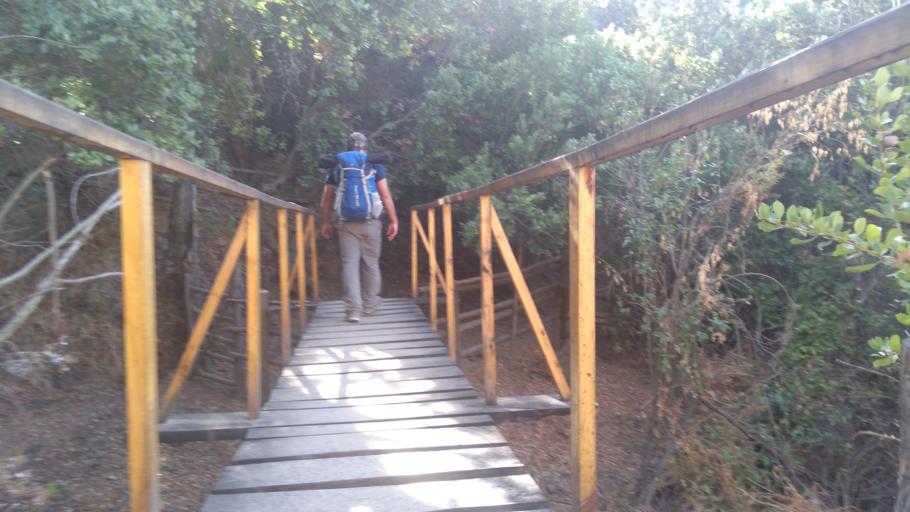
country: CL
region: Santiago Metropolitan
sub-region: Provincia de Cordillera
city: Puente Alto
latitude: -33.7238
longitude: -70.4684
